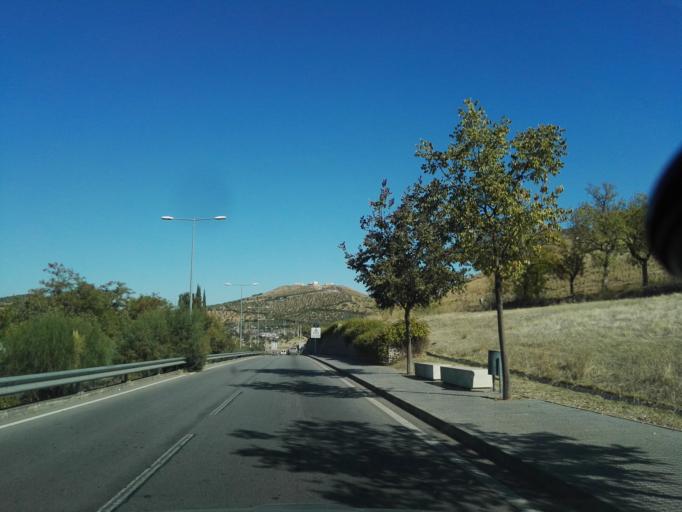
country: PT
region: Portalegre
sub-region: Elvas
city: Elvas
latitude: 38.8797
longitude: -7.1720
